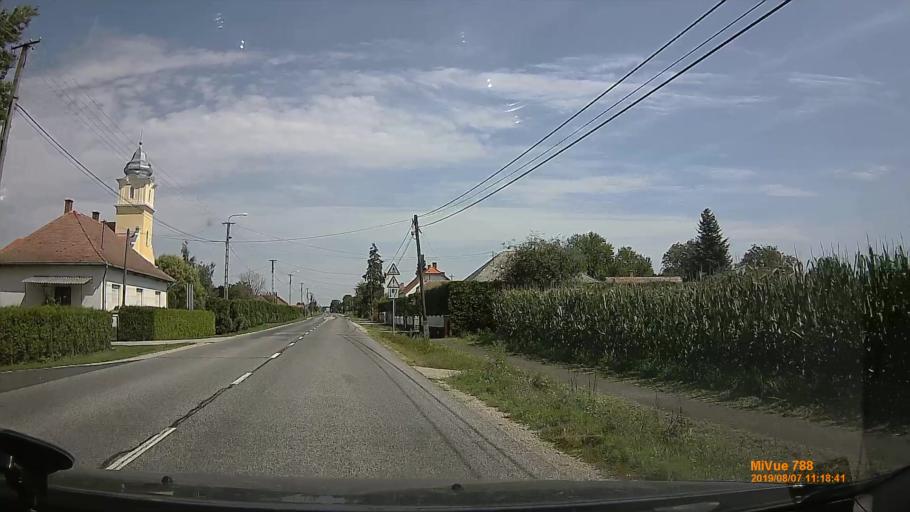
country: HU
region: Zala
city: Zalalovo
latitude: 46.7560
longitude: 16.5611
